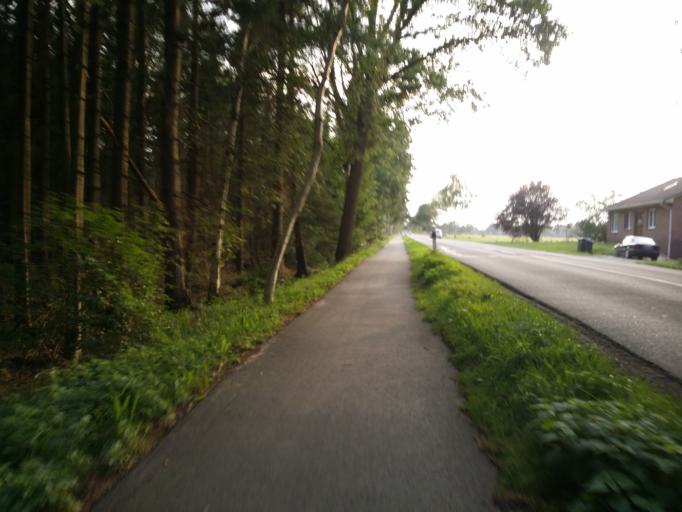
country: DE
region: Lower Saxony
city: Sandbostel
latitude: 53.4391
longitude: 9.0854
